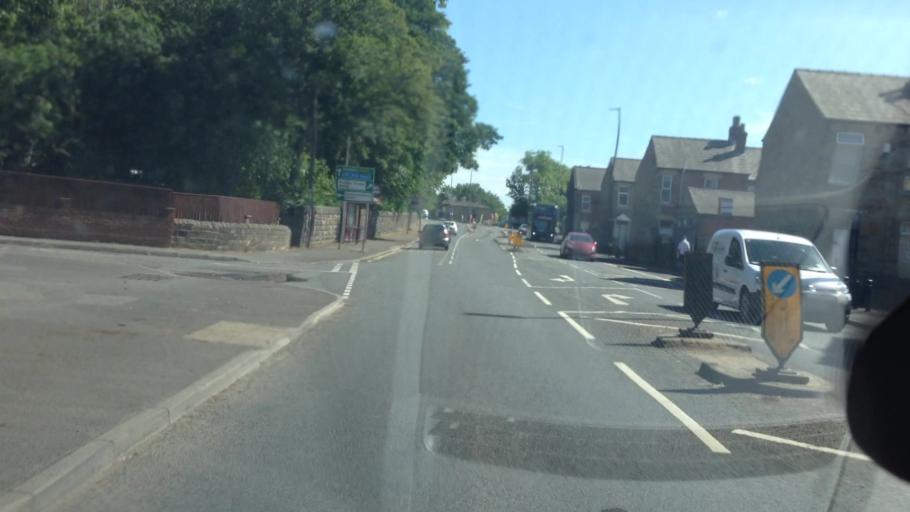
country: GB
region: England
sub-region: Kirklees
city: Dewsbury
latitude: 53.6839
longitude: -1.6469
